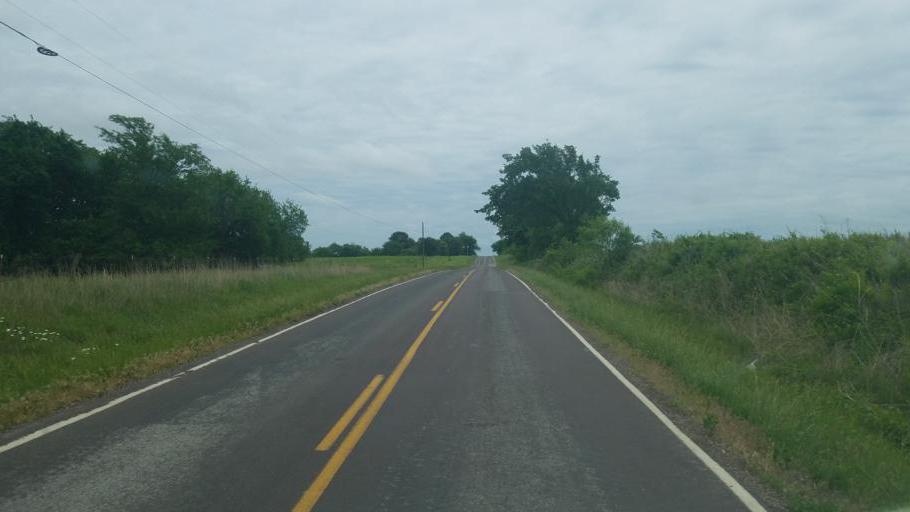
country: US
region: Missouri
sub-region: Morgan County
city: Versailles
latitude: 38.5073
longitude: -92.7861
